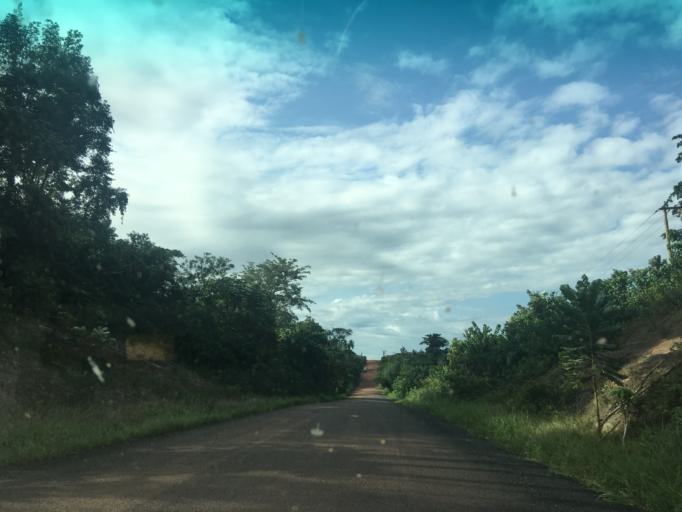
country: GH
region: Western
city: Wassa-Akropong
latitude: 5.9782
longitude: -2.4155
